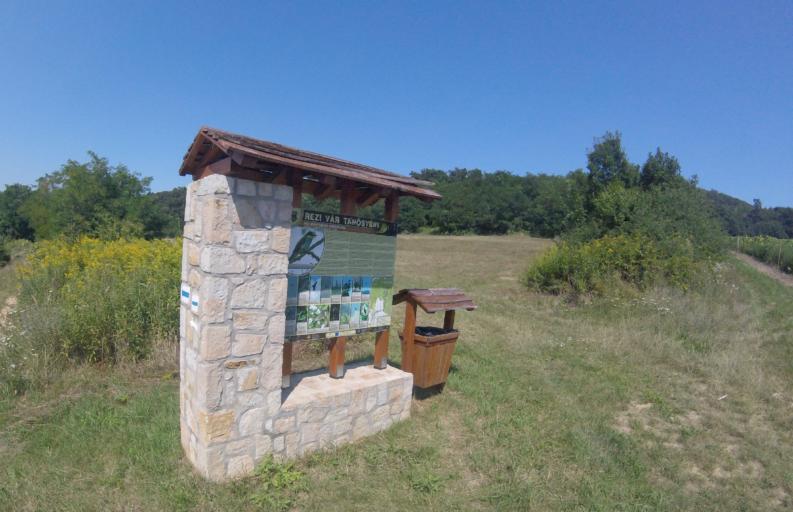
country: HU
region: Zala
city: Cserszegtomaj
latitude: 46.8558
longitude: 17.2300
